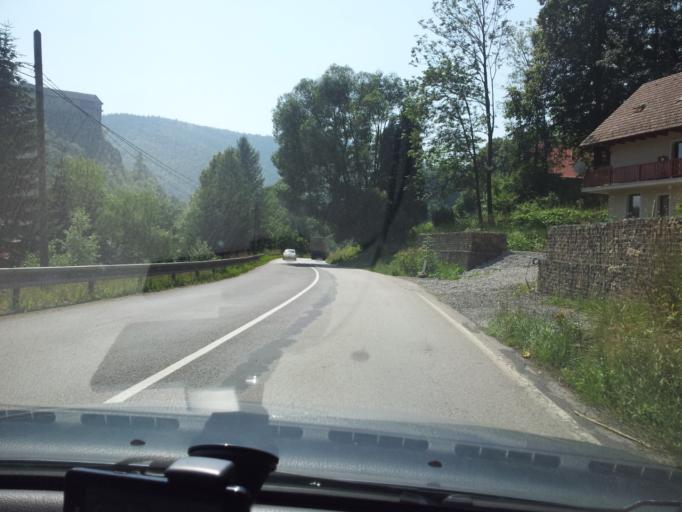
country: SK
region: Zilinsky
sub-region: Okres Dolny Kubin
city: Dolny Kubin
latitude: 49.2653
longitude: 19.3552
